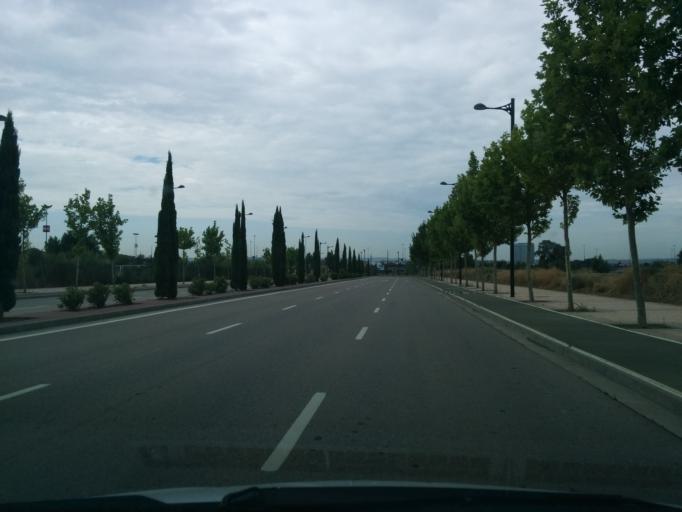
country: ES
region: Aragon
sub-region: Provincia de Zaragoza
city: Almozara
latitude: 41.6840
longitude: -0.8976
